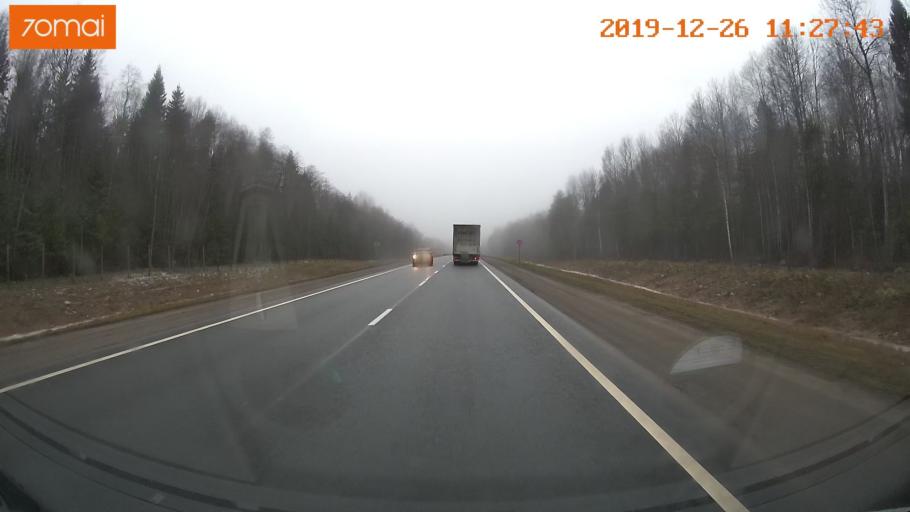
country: RU
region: Vologda
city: Chebsara
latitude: 59.1524
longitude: 38.8301
